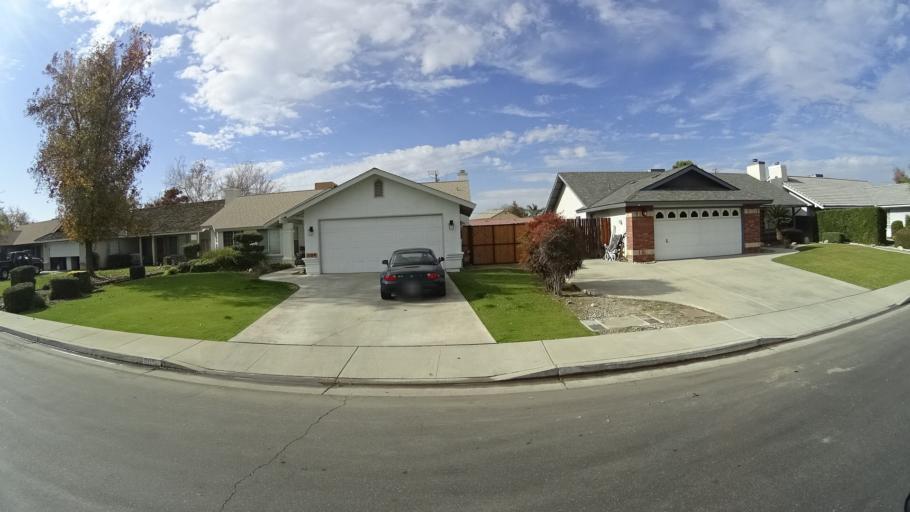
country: US
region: California
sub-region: Kern County
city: Greenacres
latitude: 35.4064
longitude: -119.1270
